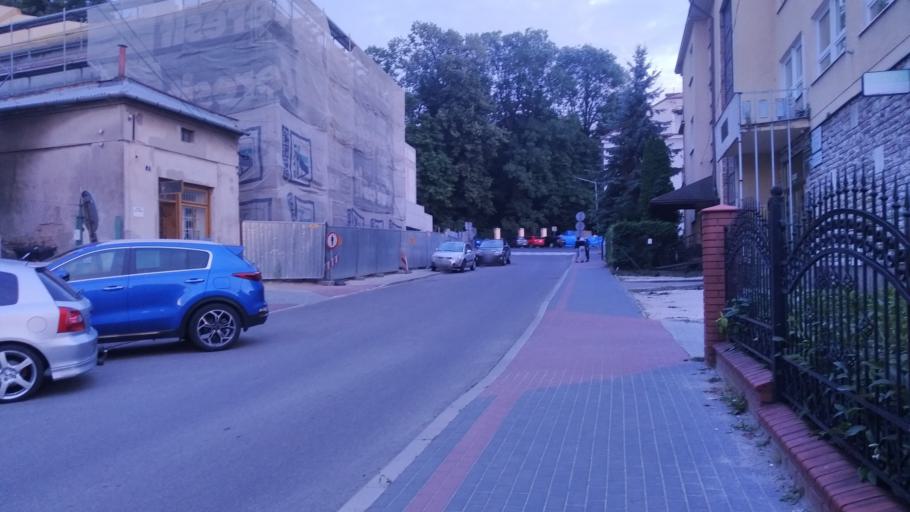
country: PL
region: Subcarpathian Voivodeship
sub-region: Powiat lancucki
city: Lancut
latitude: 50.0695
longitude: 22.2316
